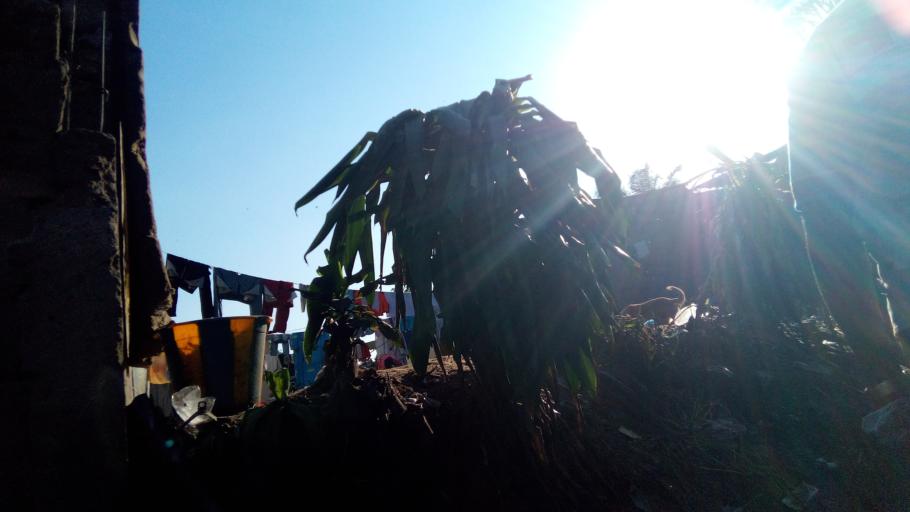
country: CD
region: Kinshasa
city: Kinshasa
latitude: -4.3690
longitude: 15.2761
